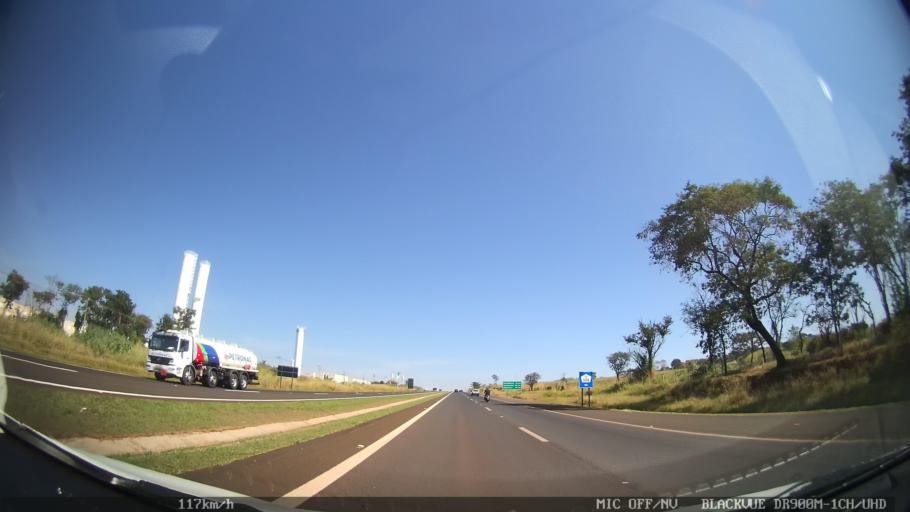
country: BR
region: Sao Paulo
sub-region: Ribeirao Preto
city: Ribeirao Preto
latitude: -21.1098
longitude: -47.8155
